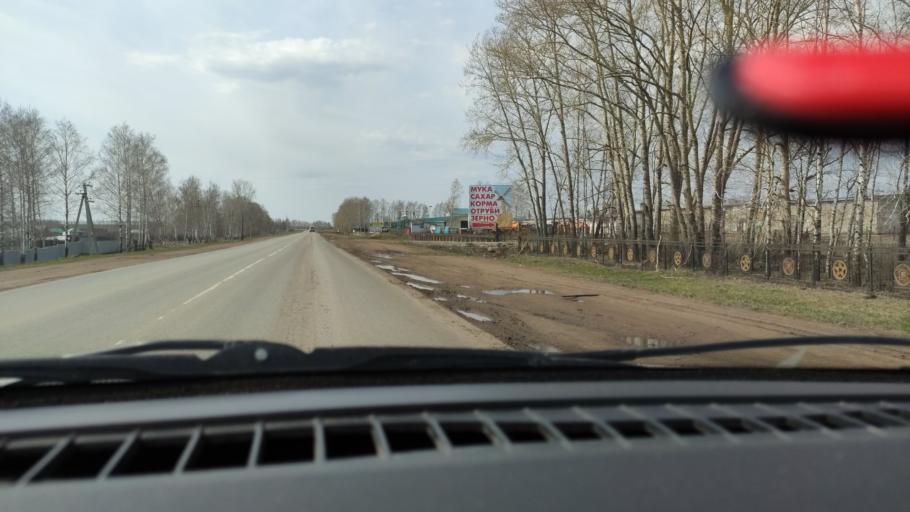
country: RU
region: Bashkortostan
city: Dyurtyuli
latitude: 55.4908
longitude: 54.8012
